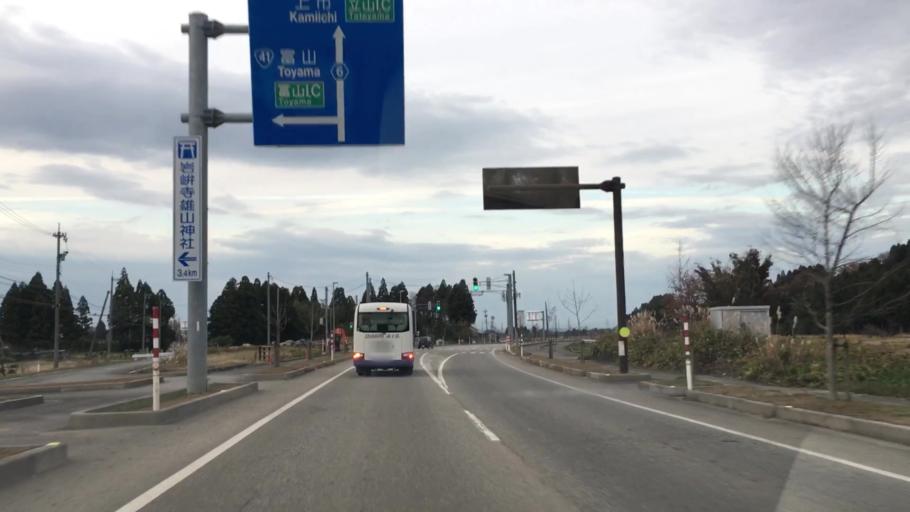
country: JP
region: Toyama
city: Kamiichi
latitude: 36.5931
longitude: 137.3280
